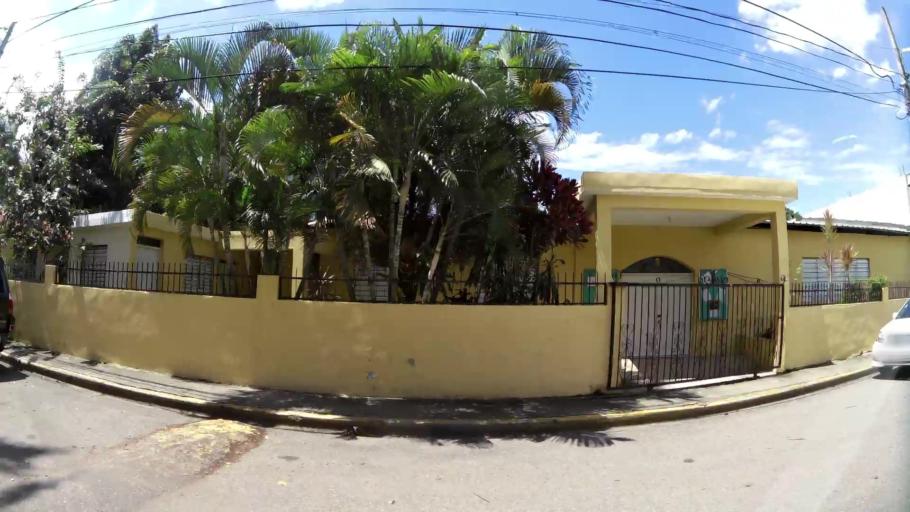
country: DO
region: Santiago
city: Santiago de los Caballeros
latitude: 19.4626
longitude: -70.6653
